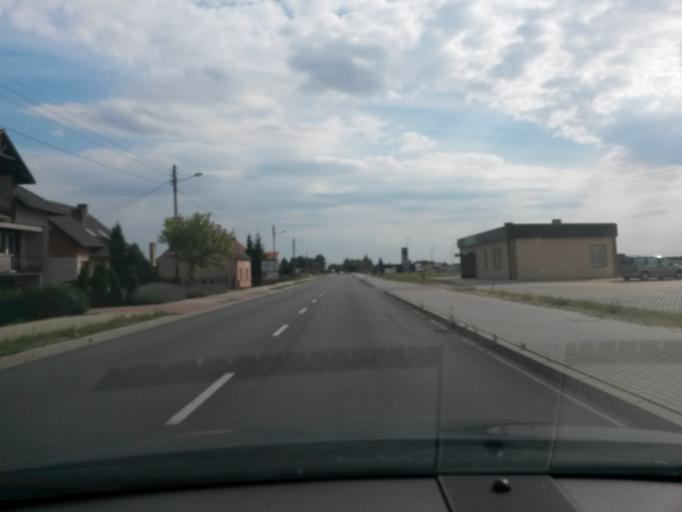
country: PL
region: Greater Poland Voivodeship
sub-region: Powiat gostynski
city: Krobia
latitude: 51.7669
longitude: 16.9725
